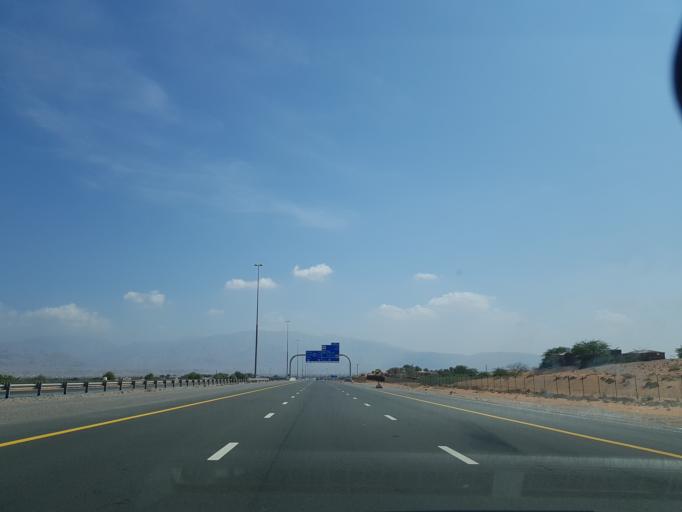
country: AE
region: Ra's al Khaymah
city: Ras al-Khaimah
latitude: 25.7049
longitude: 55.9502
